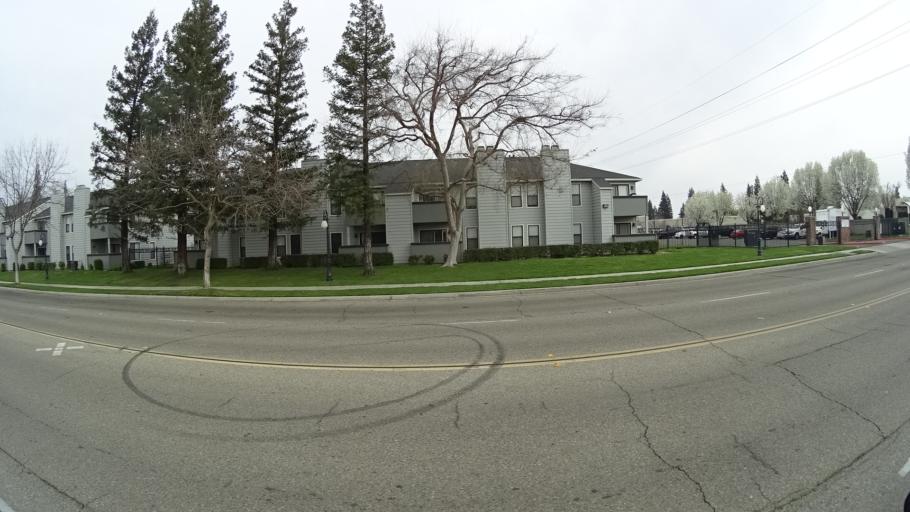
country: US
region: California
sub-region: Fresno County
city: Clovis
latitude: 36.8506
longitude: -119.8019
